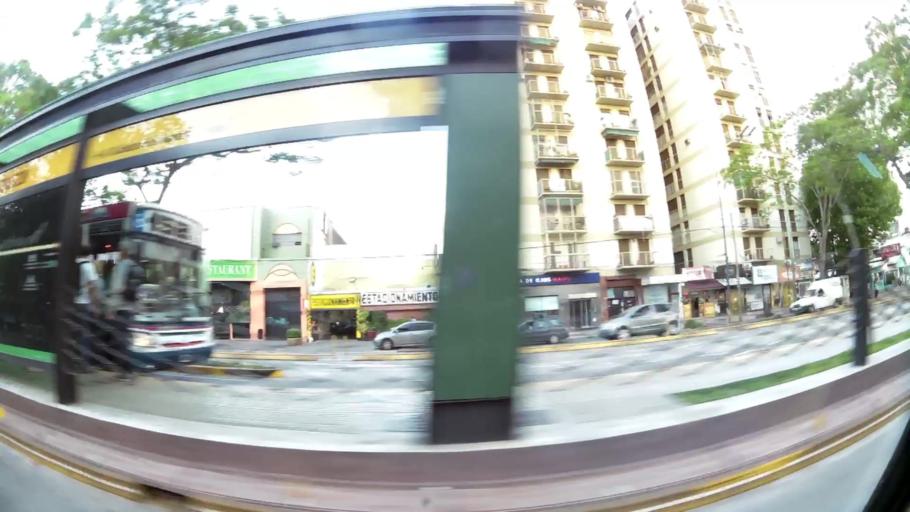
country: AR
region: Buenos Aires
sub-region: Partido de Vicente Lopez
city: Olivos
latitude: -34.5264
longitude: -58.4825
